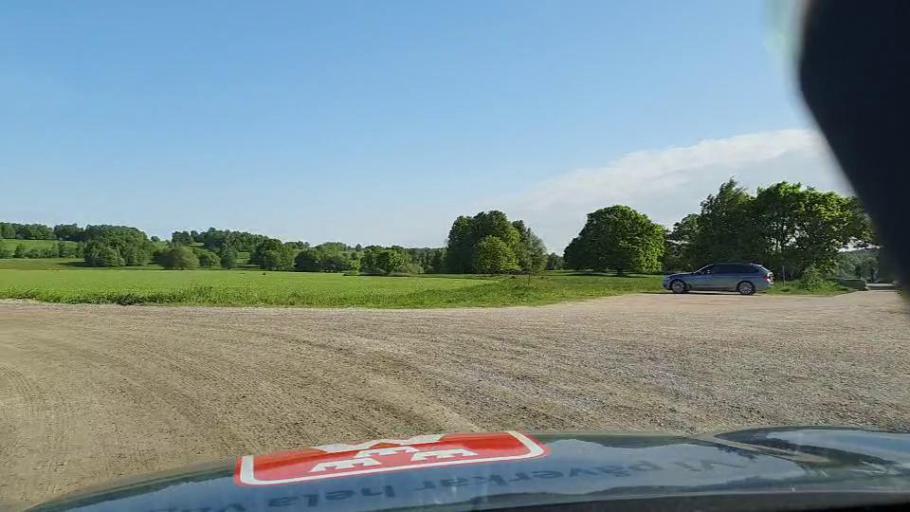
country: SE
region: Skane
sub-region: Hassleholms Kommun
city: Tormestorp
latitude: 56.1136
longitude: 13.7185
